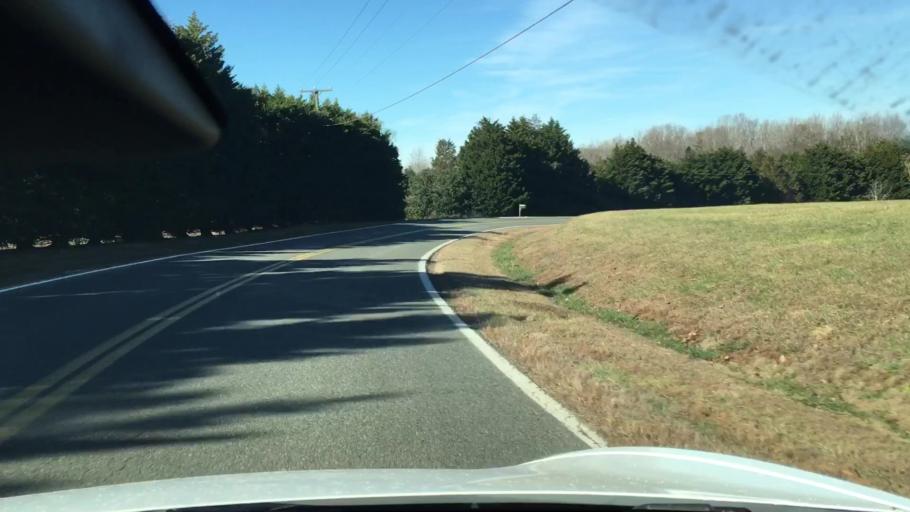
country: US
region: Virginia
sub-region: Powhatan County
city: Powhatan
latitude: 37.5511
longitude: -77.7956
